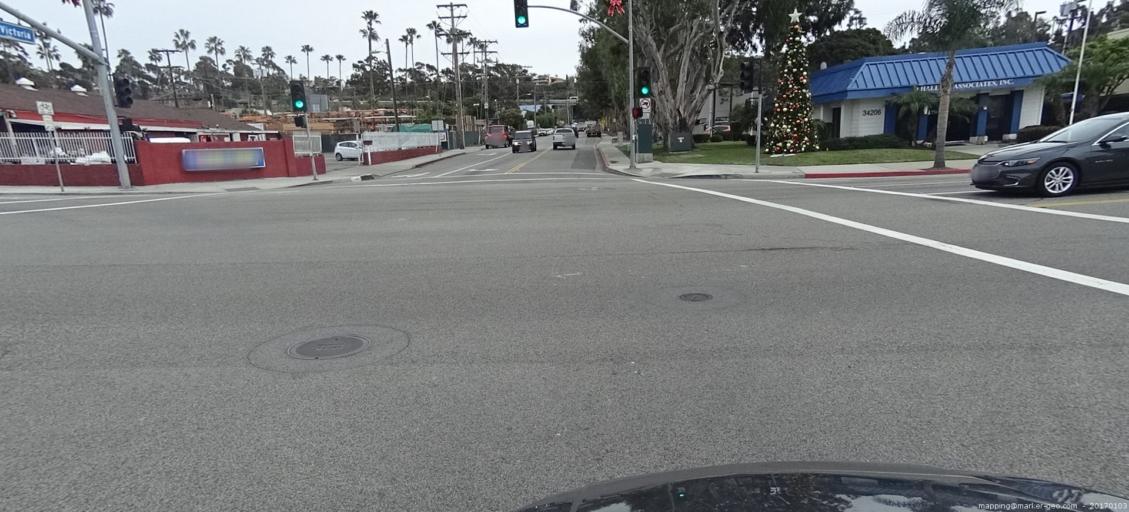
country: US
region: California
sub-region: Orange County
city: Dana Point
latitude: 33.4665
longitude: -117.6776
